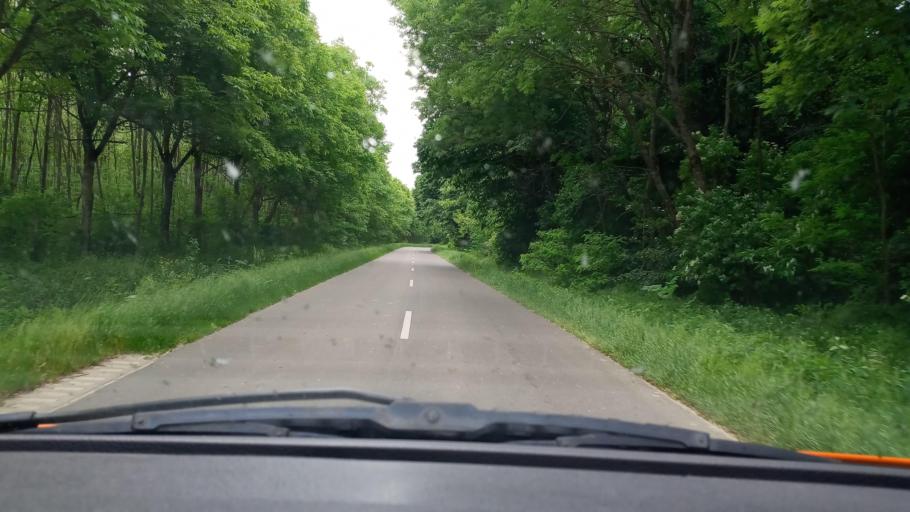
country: HU
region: Baranya
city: Vajszlo
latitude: 45.8329
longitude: 17.9725
